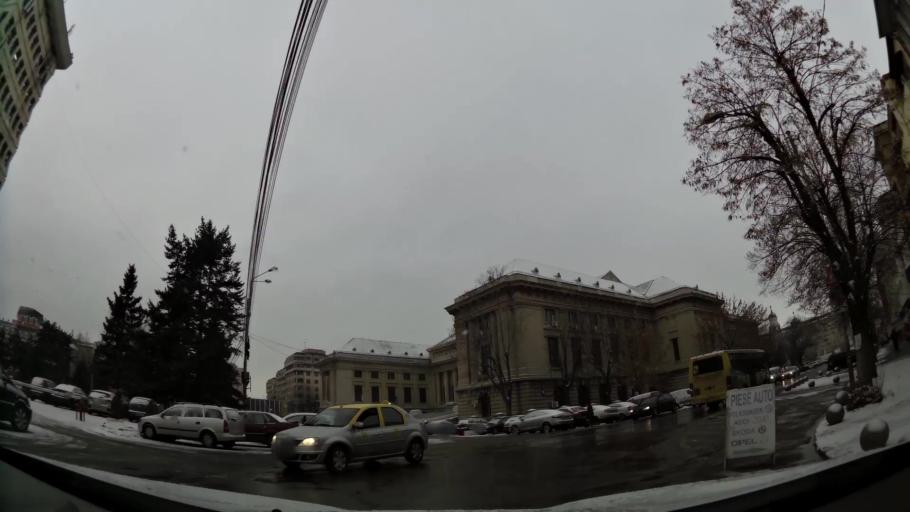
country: RO
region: Prahova
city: Ploiesti
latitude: 44.9422
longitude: 26.0230
